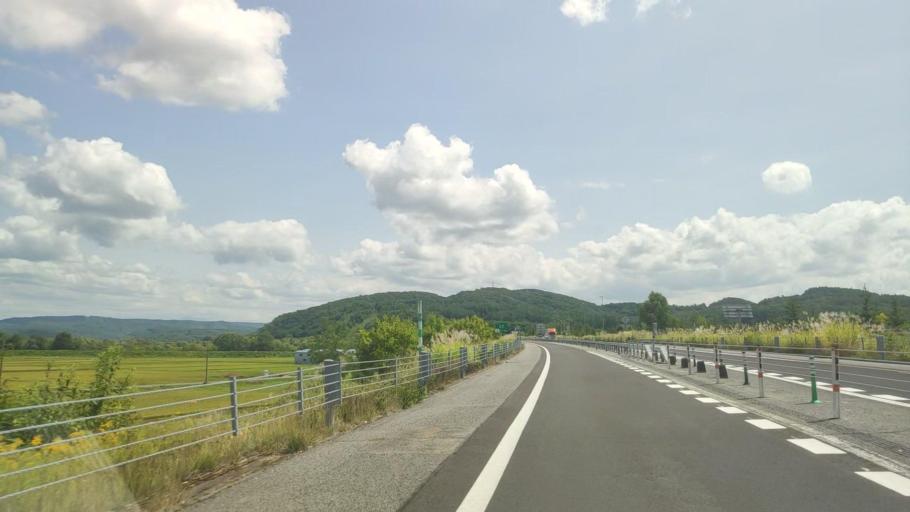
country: JP
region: Hokkaido
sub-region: Asahikawa-shi
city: Asahikawa
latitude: 43.9016
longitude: 142.5505
